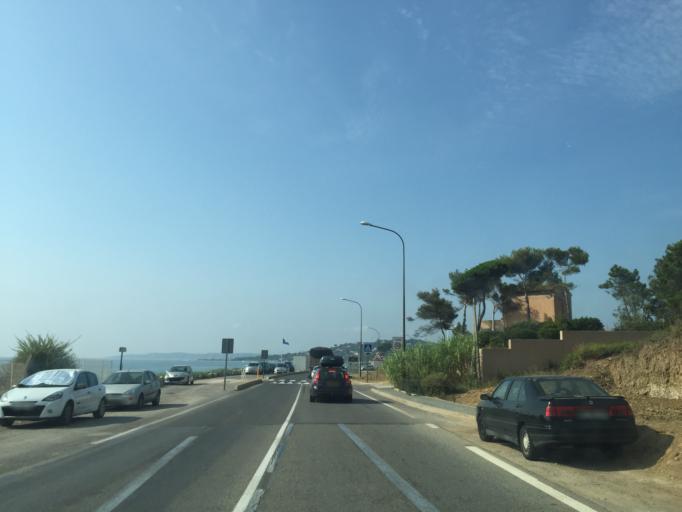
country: FR
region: Provence-Alpes-Cote d'Azur
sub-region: Departement du Var
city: Sainte-Maxime
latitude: 43.3322
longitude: 6.6686
